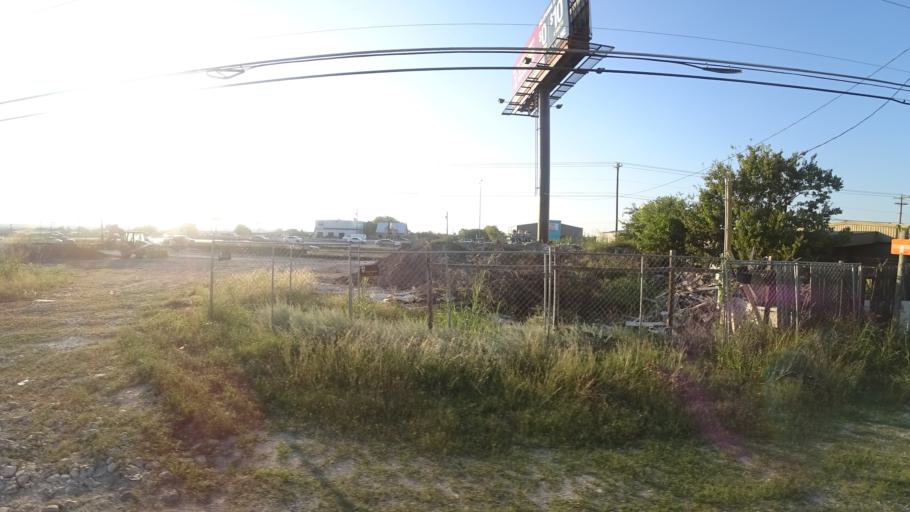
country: US
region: Texas
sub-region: Travis County
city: Wells Branch
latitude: 30.3679
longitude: -97.6808
